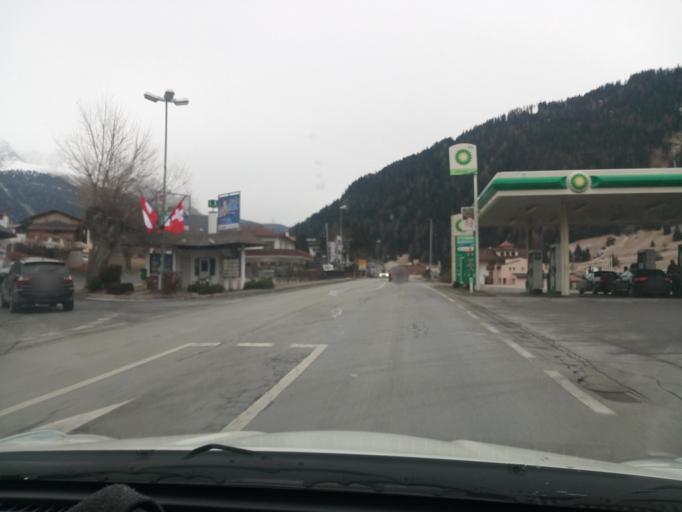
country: AT
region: Tyrol
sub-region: Politischer Bezirk Landeck
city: Nauders
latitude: 46.8948
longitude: 10.4986
